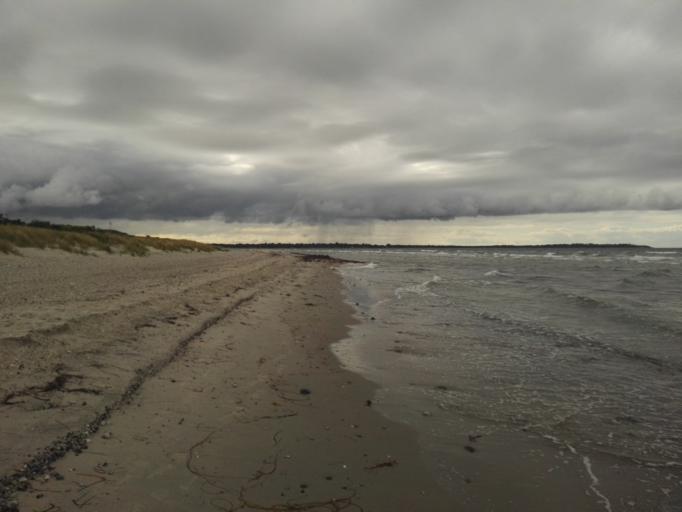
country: DK
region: Zealand
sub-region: Odsherred Kommune
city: Nykobing Sjaelland
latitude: 55.9449
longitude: 11.6751
